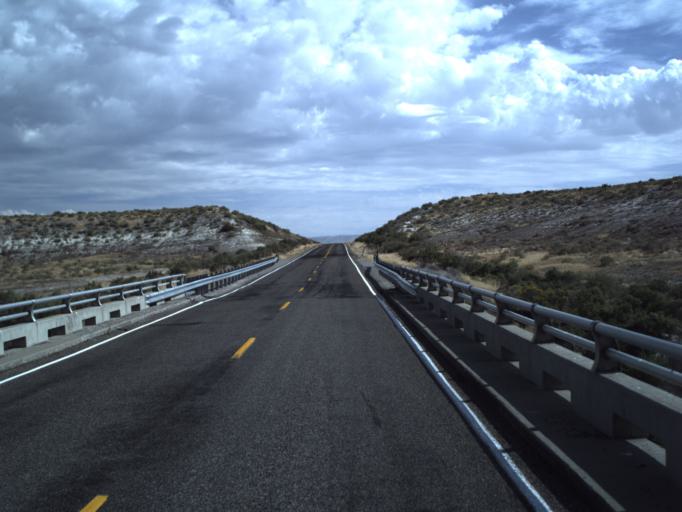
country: US
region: Utah
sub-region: Tooele County
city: Wendover
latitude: 41.4073
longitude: -113.9361
